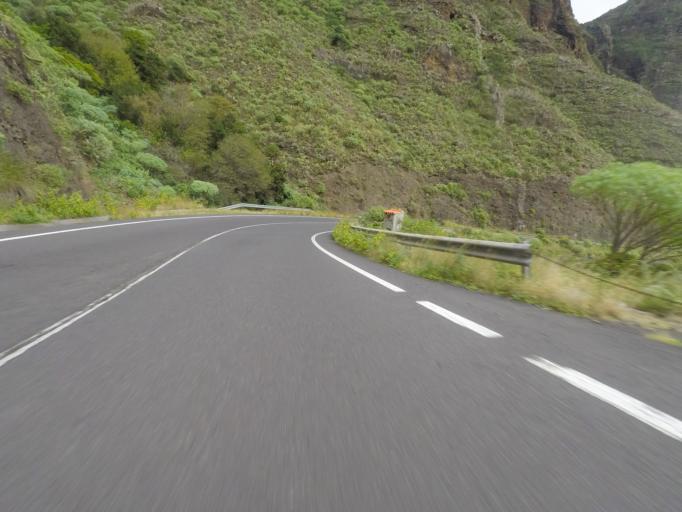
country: ES
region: Canary Islands
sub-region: Provincia de Santa Cruz de Tenerife
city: Hermigua
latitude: 28.1323
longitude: -17.1808
